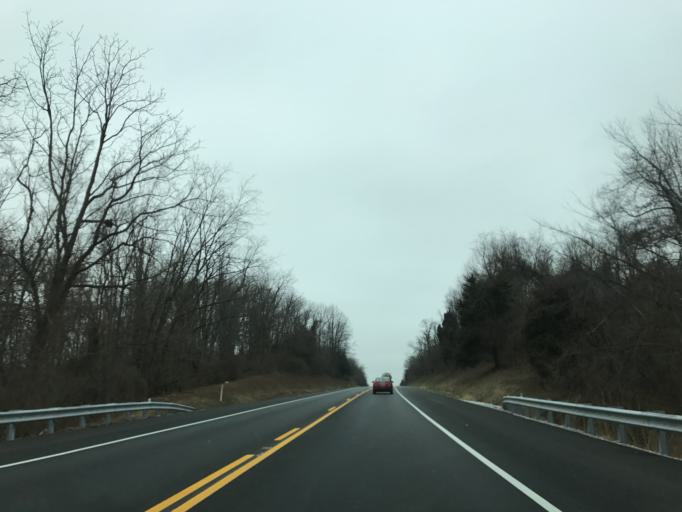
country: US
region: Maryland
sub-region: Carroll County
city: New Windsor
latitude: 39.6096
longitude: -77.0712
